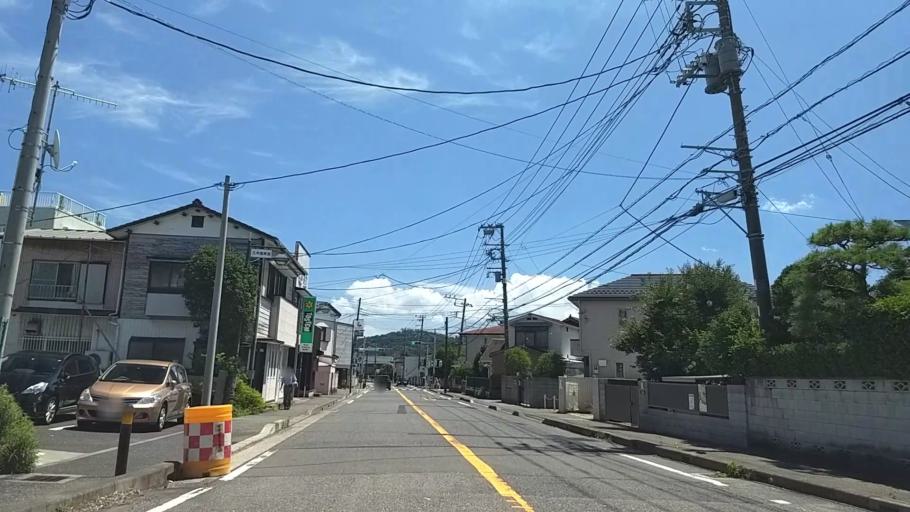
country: JP
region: Kanagawa
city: Zushi
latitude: 35.3010
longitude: 139.5706
